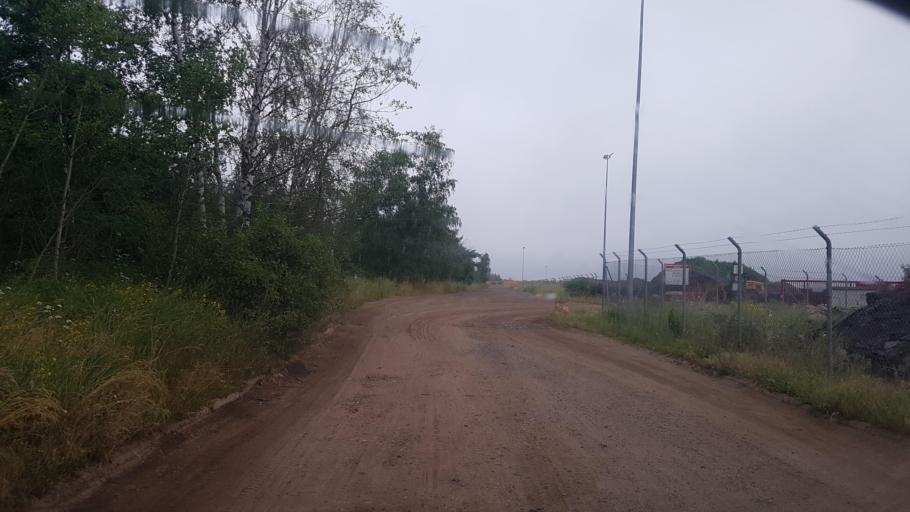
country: DE
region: Brandenburg
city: Lauchhammer
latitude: 51.5428
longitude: 13.7476
